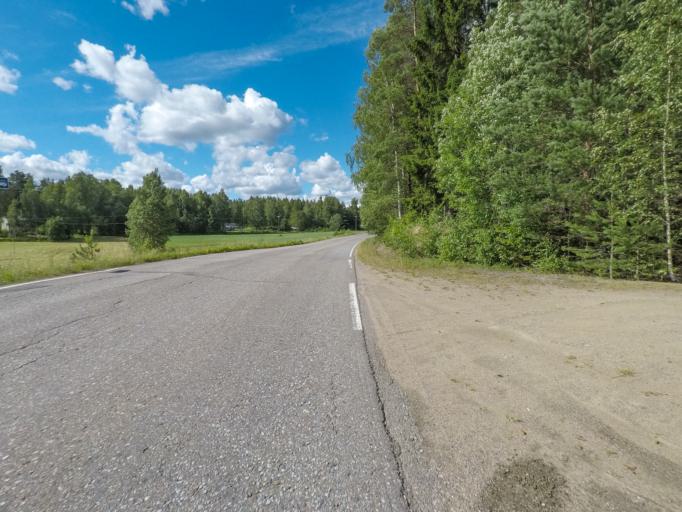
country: FI
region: South Karelia
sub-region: Lappeenranta
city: Joutseno
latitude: 61.1099
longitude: 28.3695
